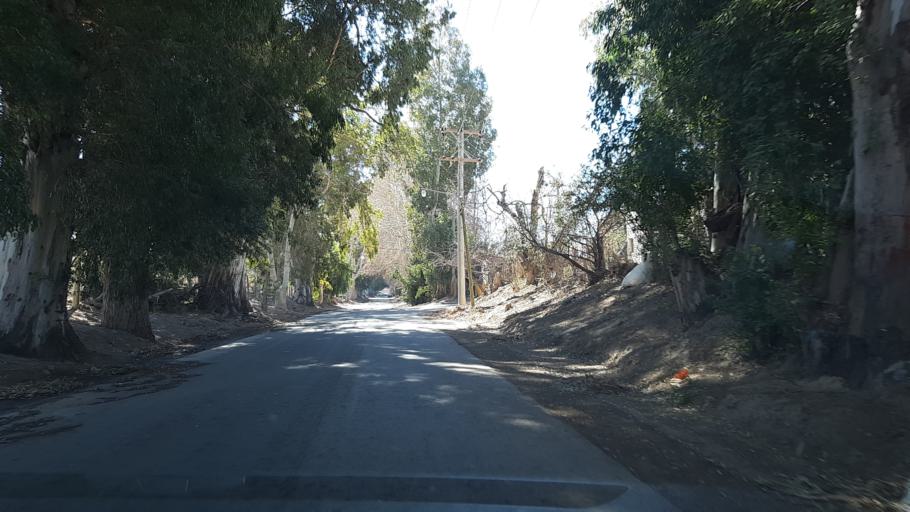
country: AR
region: San Juan
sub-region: Departamento de Zonda
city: Zonda
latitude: -31.5660
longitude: -68.7348
